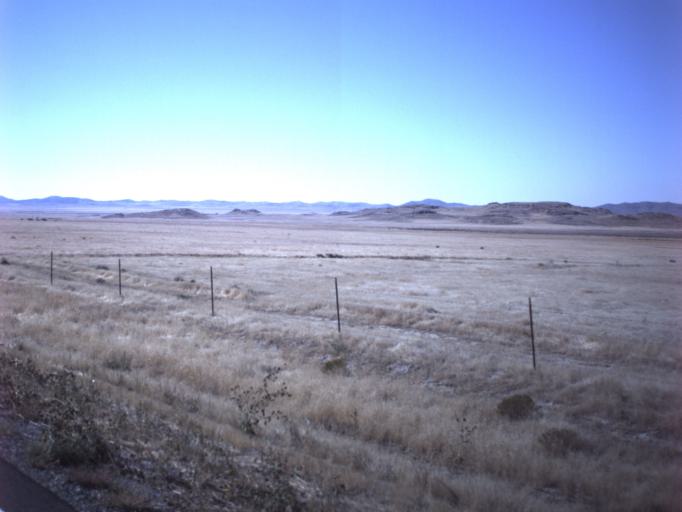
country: US
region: Utah
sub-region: Tooele County
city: Grantsville
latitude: 40.4099
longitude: -112.7484
